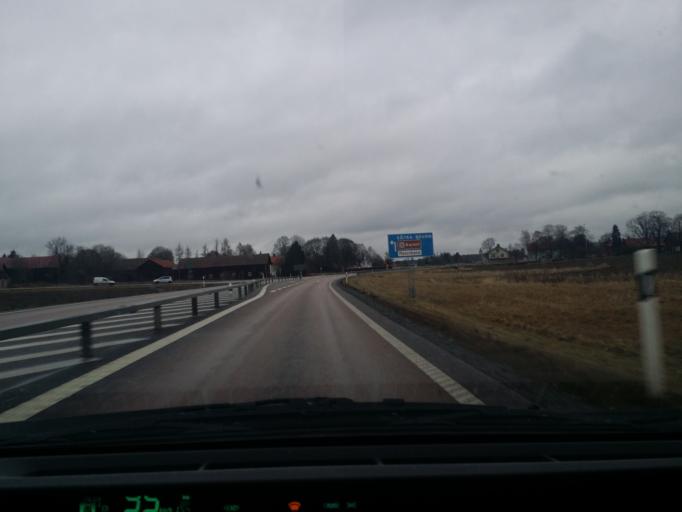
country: SE
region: Vaestmanland
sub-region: Sala Kommun
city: Sala
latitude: 59.8540
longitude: 16.5357
